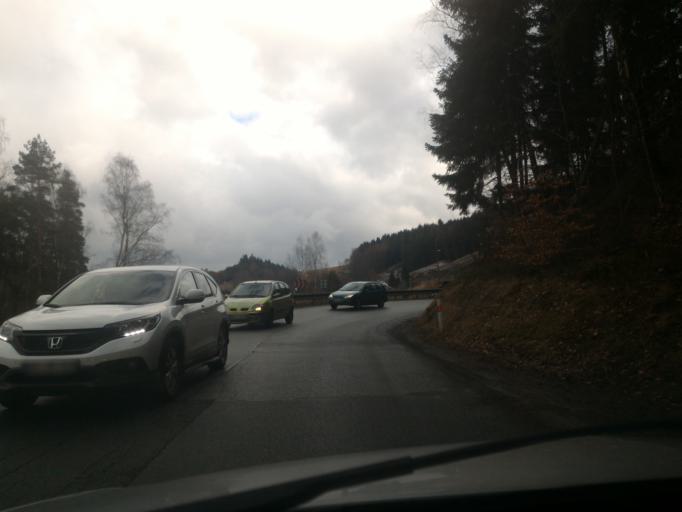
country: CZ
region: Liberecky
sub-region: Okres Jablonec nad Nisou
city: Janov nad Nisou
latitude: 50.7491
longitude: 15.1197
